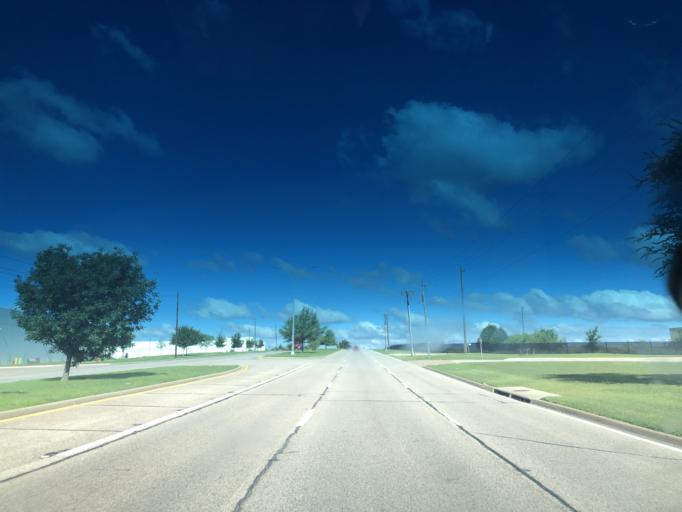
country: US
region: Texas
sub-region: Dallas County
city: Grand Prairie
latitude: 32.7103
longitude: -97.0271
